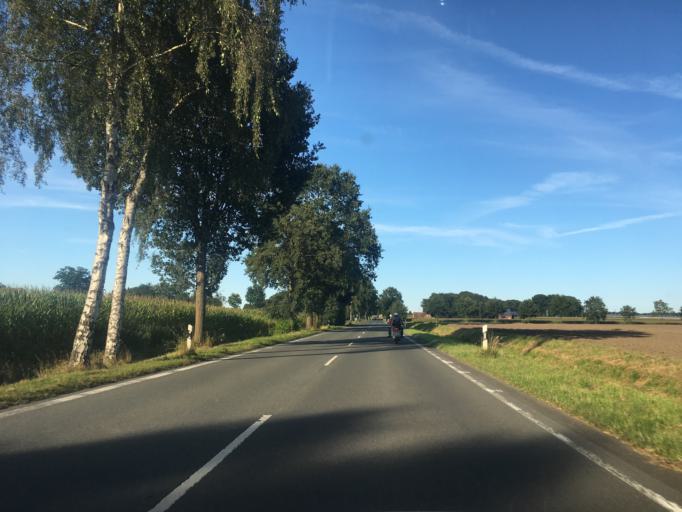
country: DE
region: North Rhine-Westphalia
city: Olfen
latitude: 51.7761
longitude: 7.3493
